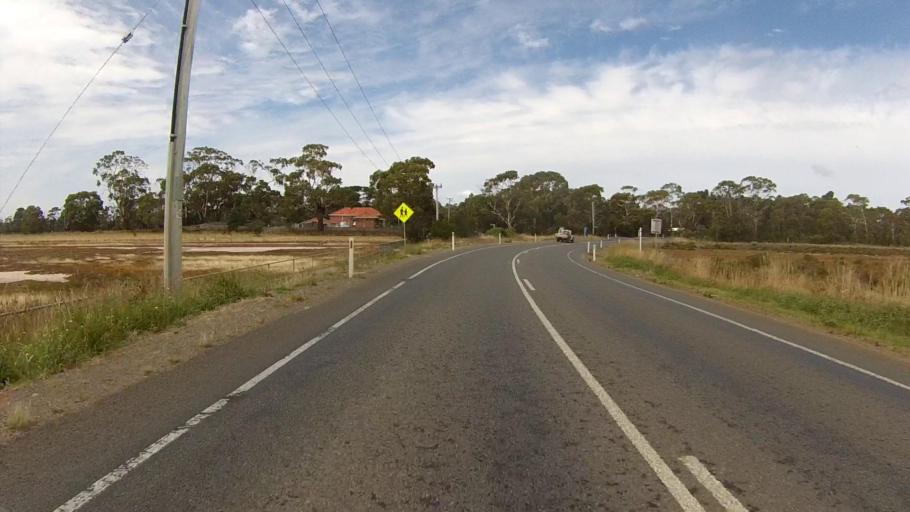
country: AU
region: Tasmania
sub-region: Clarence
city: Sandford
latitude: -42.9269
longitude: 147.4914
